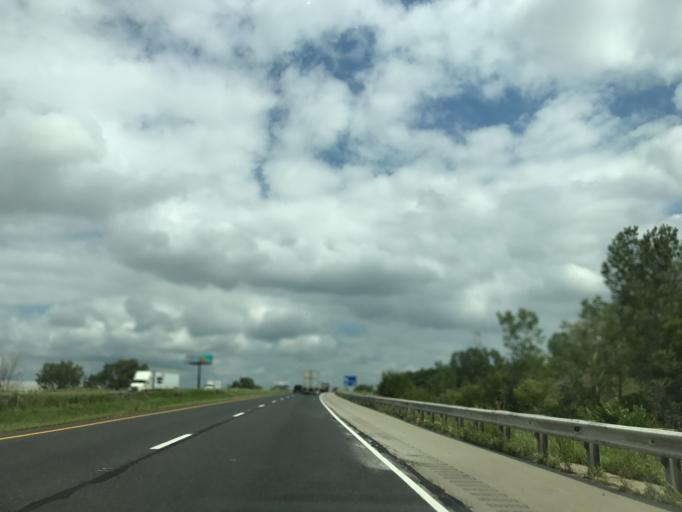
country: US
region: Illinois
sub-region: Will County
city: Rockdale
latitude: 41.5067
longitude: -88.1485
